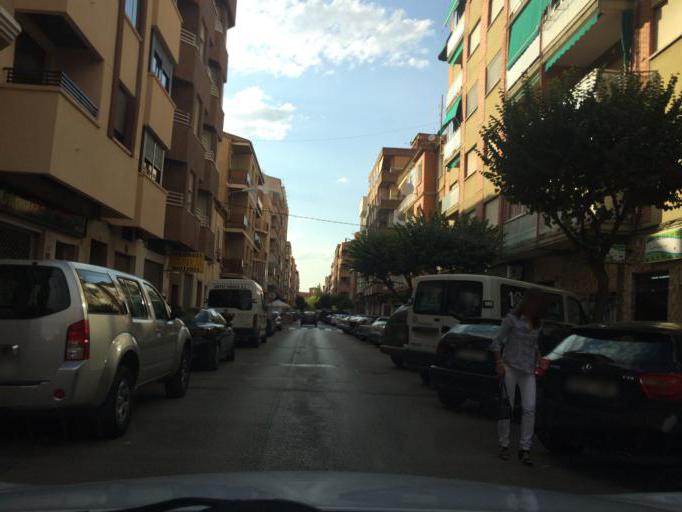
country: ES
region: Castille-La Mancha
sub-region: Provincia de Albacete
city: Albacete
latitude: 38.9904
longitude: -1.8620
